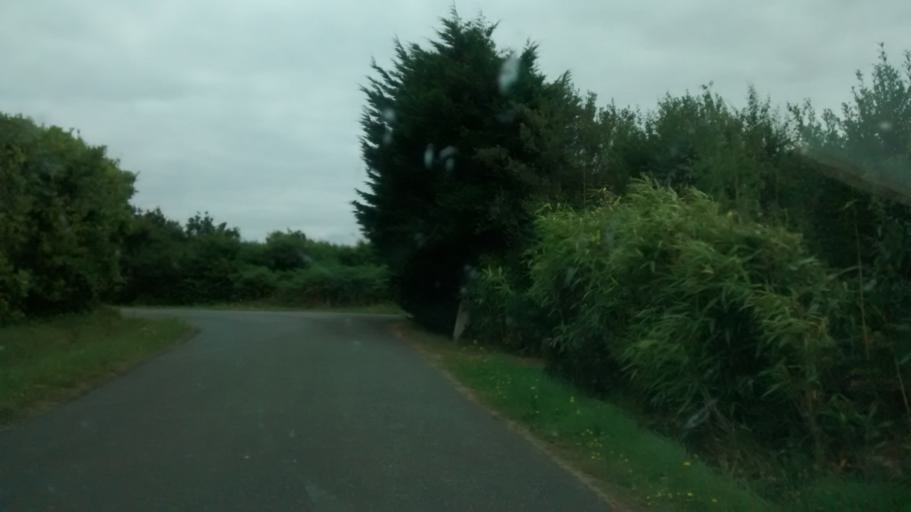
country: FR
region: Brittany
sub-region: Departement du Finistere
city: Lanveoc
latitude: 48.3317
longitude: -4.4372
